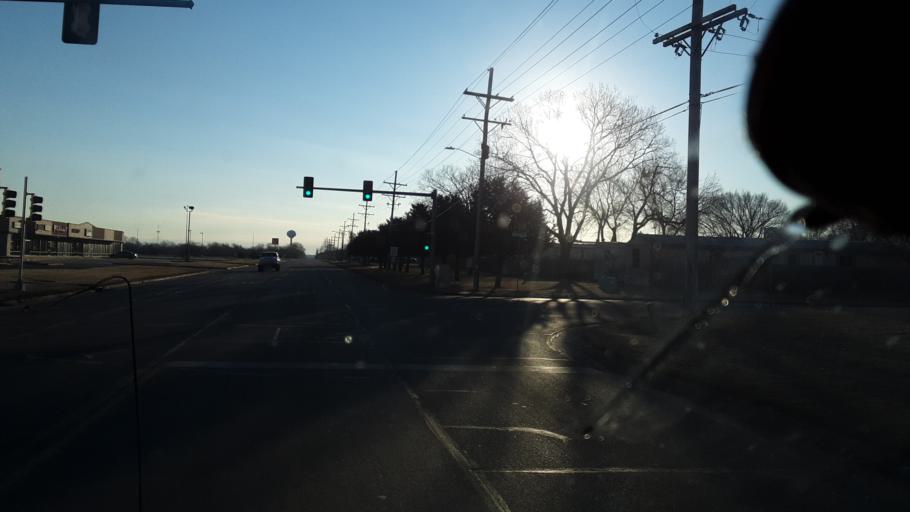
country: US
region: Kansas
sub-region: Reno County
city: Hutchinson
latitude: 38.0650
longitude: -97.8998
